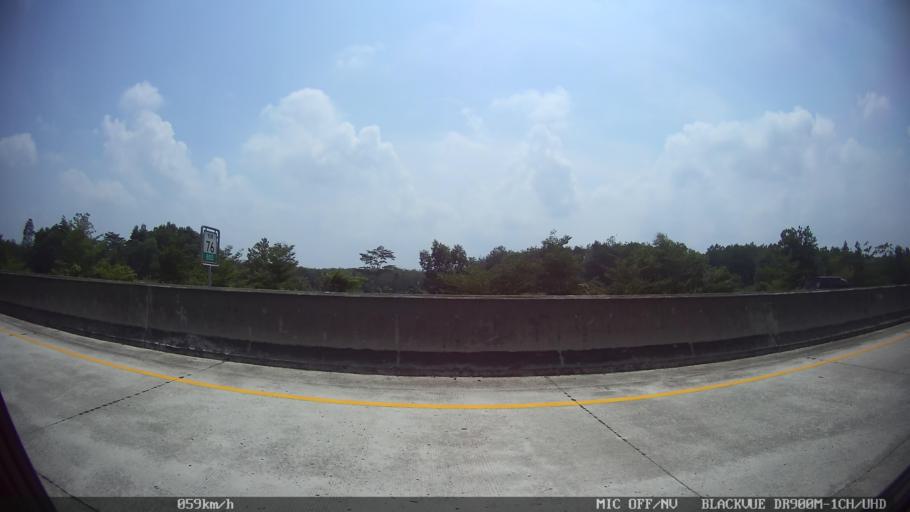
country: ID
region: Lampung
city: Kedaton
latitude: -5.3812
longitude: 105.3334
